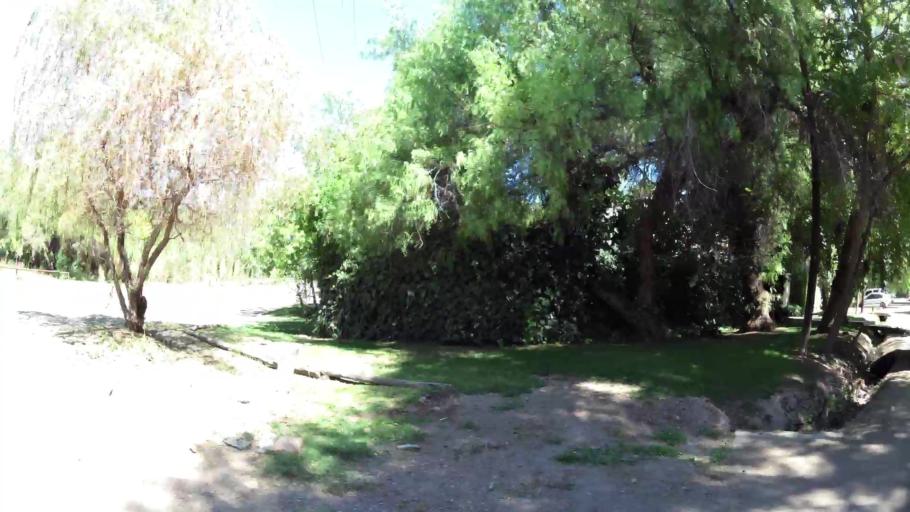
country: AR
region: Mendoza
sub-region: Departamento de Godoy Cruz
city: Godoy Cruz
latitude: -32.9638
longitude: -68.8560
